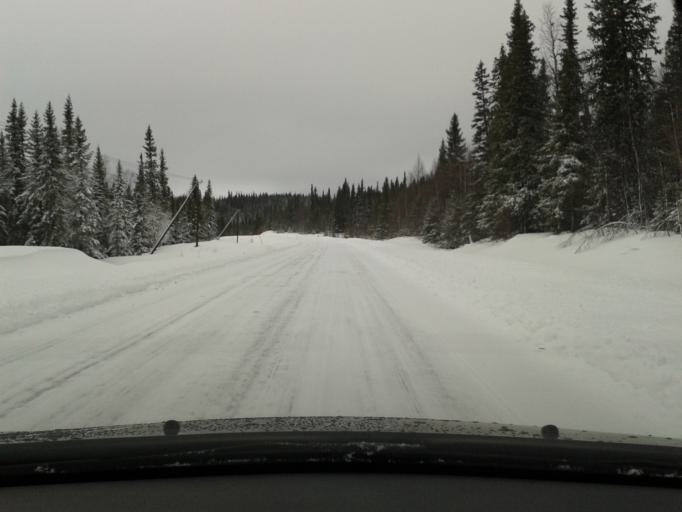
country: SE
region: Vaesterbotten
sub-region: Vilhelmina Kommun
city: Sjoberg
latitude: 65.1942
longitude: 15.9616
